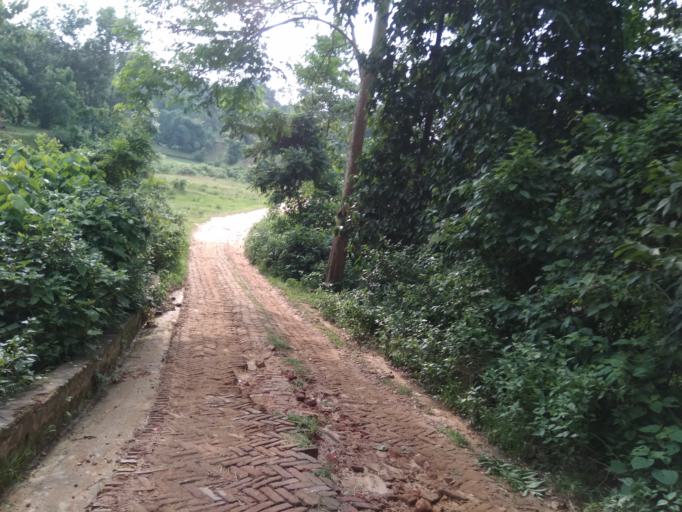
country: BD
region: Chittagong
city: Manikchari
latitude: 22.9316
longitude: 91.9114
